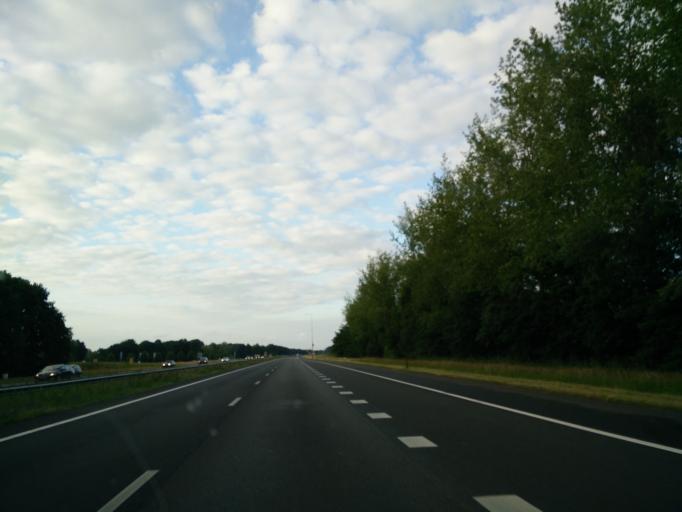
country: NL
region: Gelderland
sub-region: Gemeente Ermelo
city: Horst
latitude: 52.3134
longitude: 5.5645
